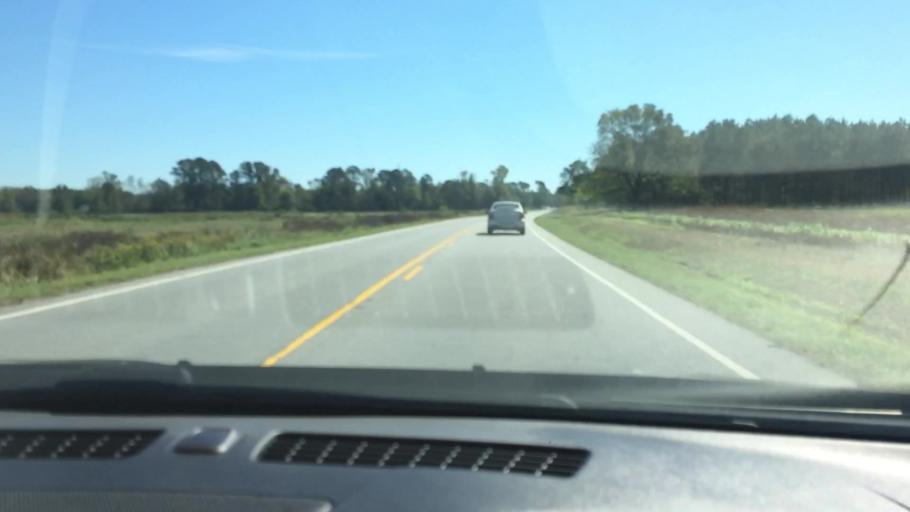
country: US
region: North Carolina
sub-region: Pitt County
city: Grifton
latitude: 35.3492
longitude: -77.3265
